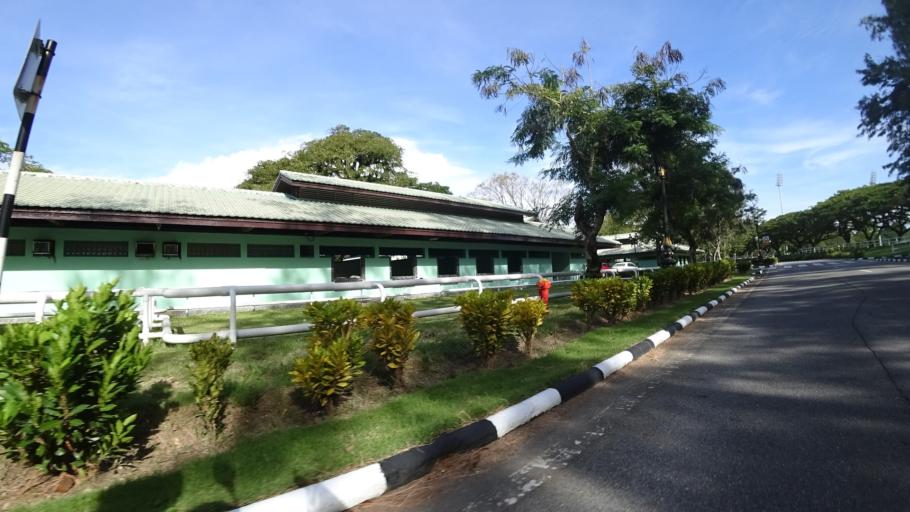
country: BN
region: Brunei and Muara
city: Bandar Seri Begawan
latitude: 4.9487
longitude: 114.8314
